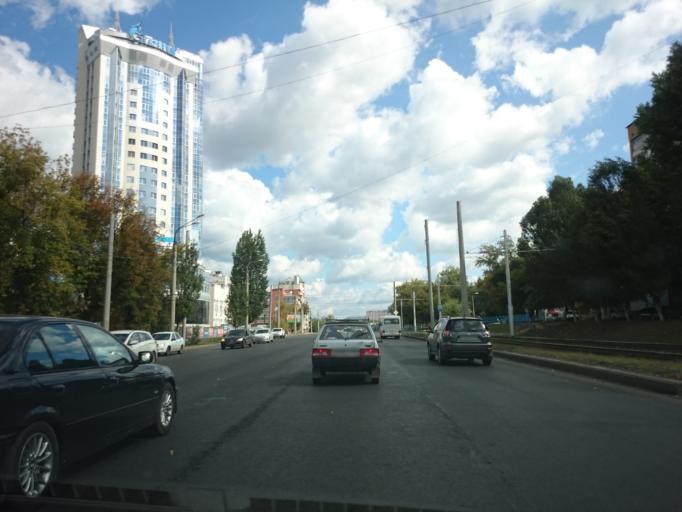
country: RU
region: Samara
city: Samara
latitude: 53.2183
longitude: 50.1527
